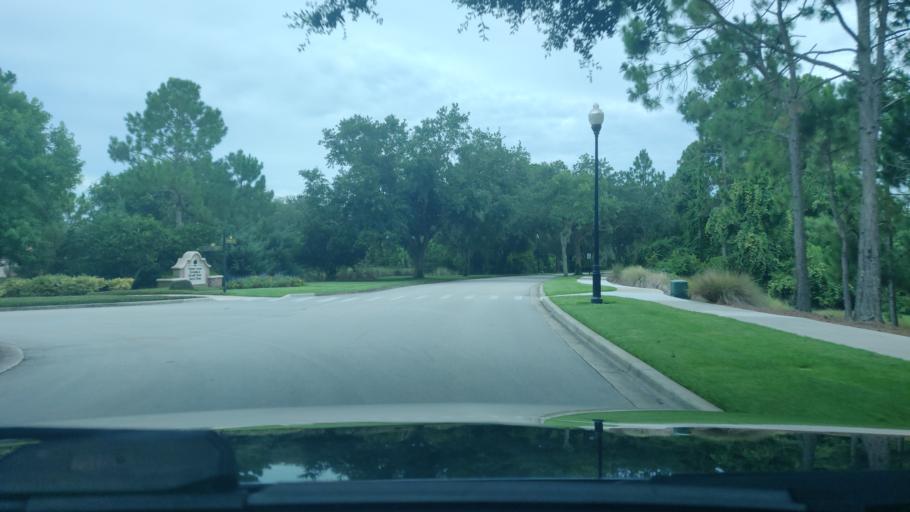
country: US
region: Florida
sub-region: Flagler County
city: Palm Coast
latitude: 29.5333
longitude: -81.1673
